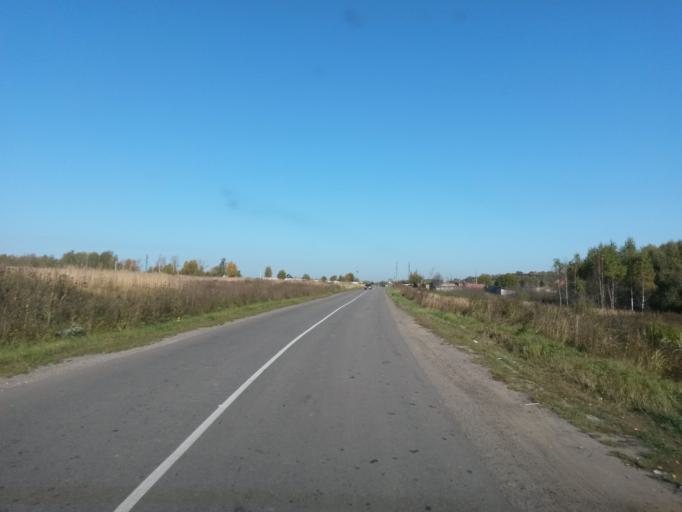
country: RU
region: Moskovskaya
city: Lyubuchany
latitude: 55.2415
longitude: 37.6179
